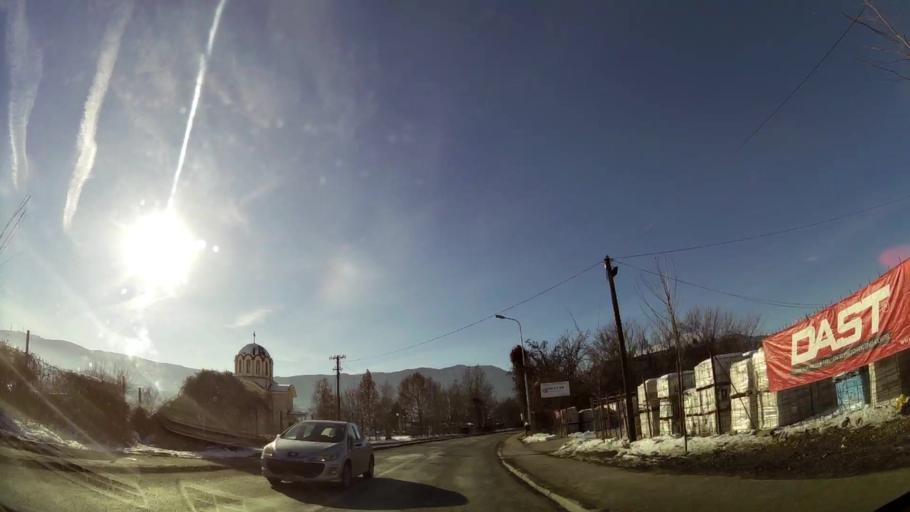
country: MK
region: Saraj
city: Saraj
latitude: 42.0048
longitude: 21.3326
